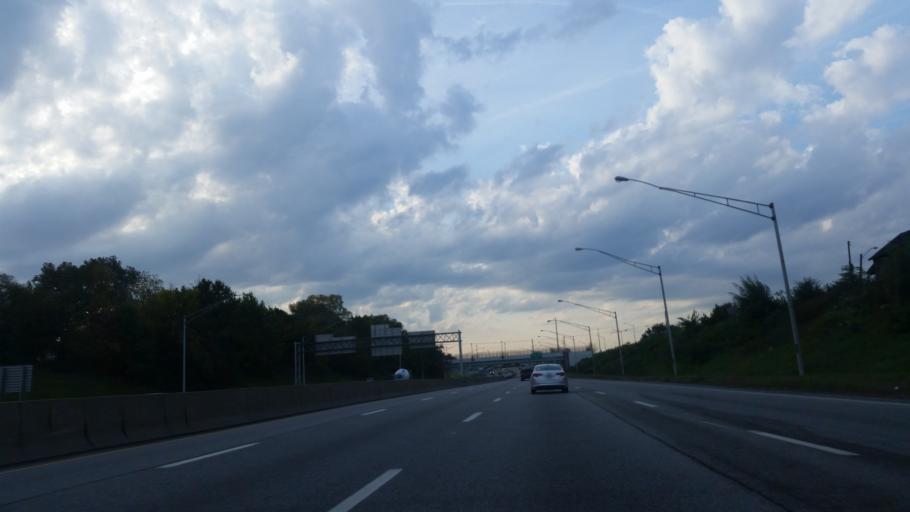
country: US
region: Ohio
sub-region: Cuyahoga County
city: Newburgh Heights
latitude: 41.4736
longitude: -81.6603
